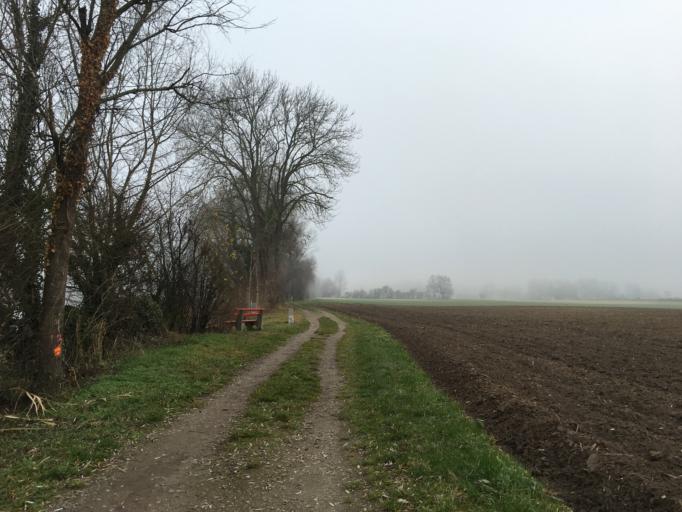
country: CH
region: Aargau
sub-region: Bezirk Zurzach
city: Bad Zurzach
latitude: 47.5984
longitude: 8.2971
